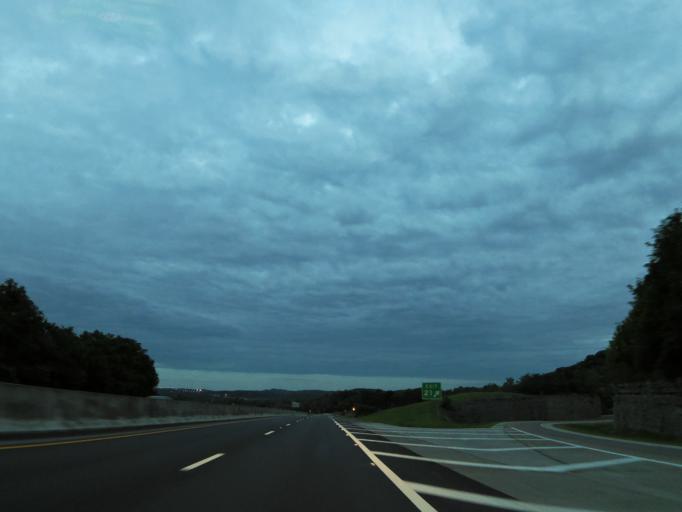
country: US
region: Tennessee
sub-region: Davidson County
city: Nashville
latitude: 36.2297
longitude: -86.8397
